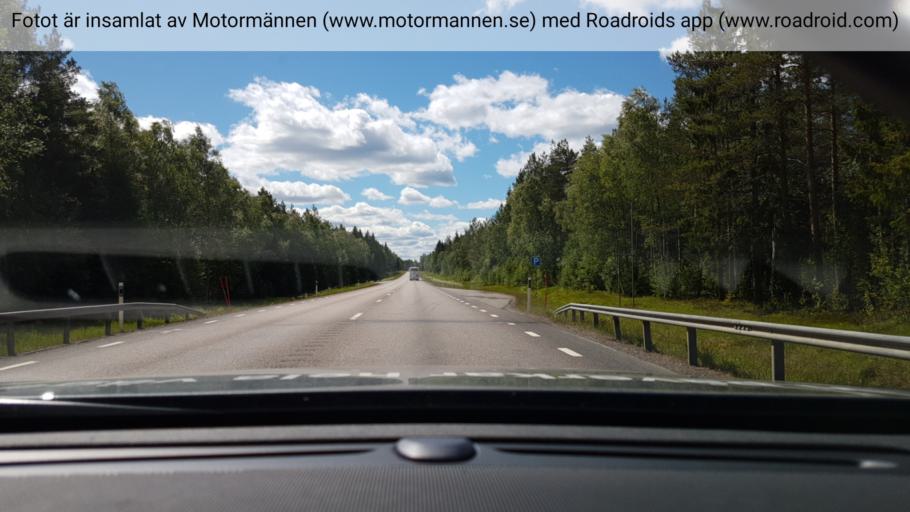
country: SE
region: Vaesterbotten
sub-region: Skelleftea Kommun
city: Burea
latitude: 64.3289
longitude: 21.1979
